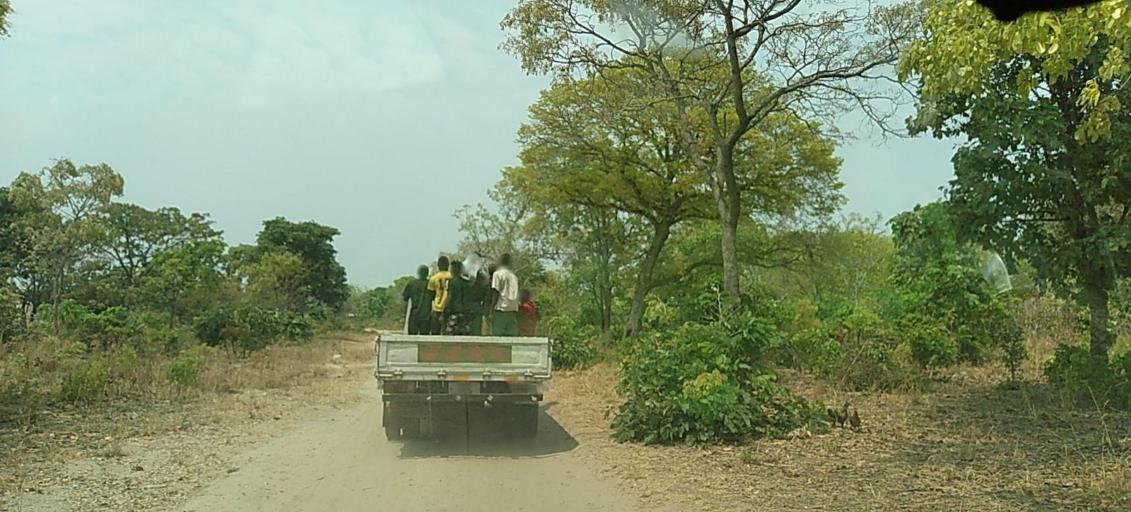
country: ZM
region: North-Western
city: Kabompo
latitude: -13.4870
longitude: 24.4614
